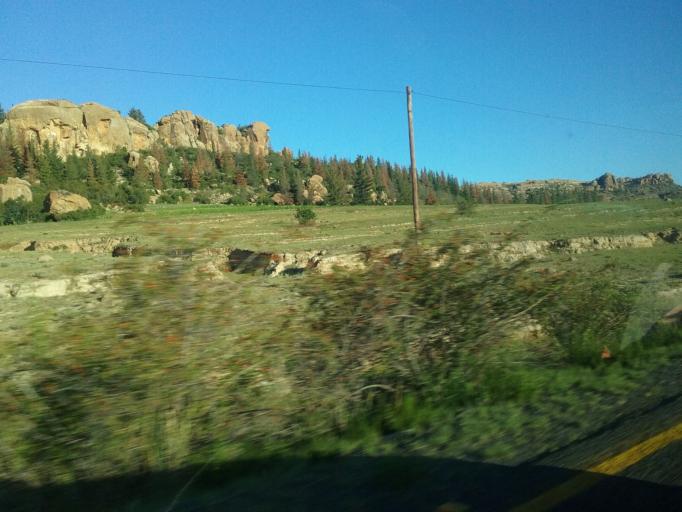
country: LS
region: Berea
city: Teyateyaneng
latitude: -29.1468
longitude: 27.6908
